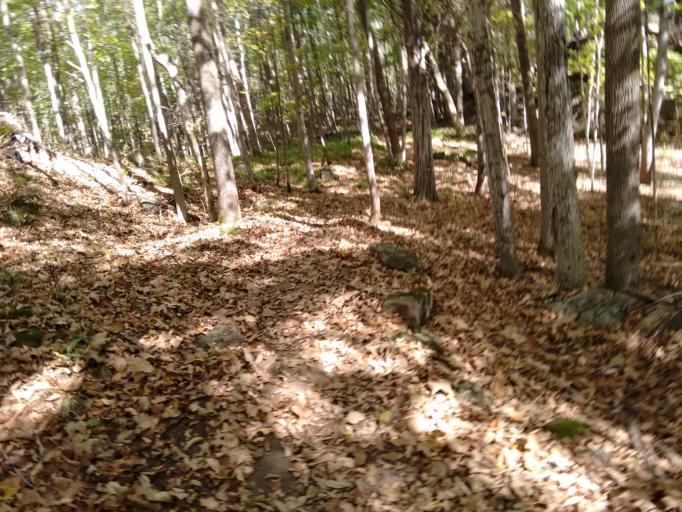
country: CA
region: Ontario
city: Kingston
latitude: 44.5065
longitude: -76.5531
